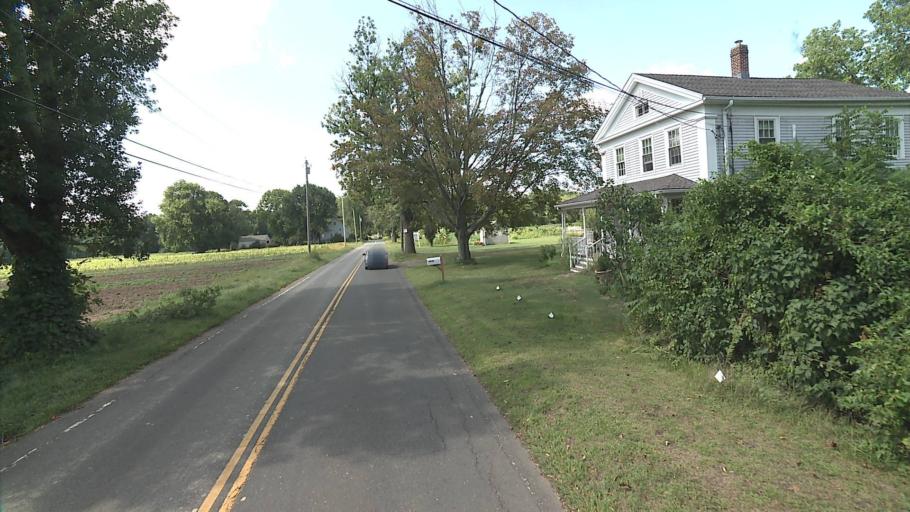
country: US
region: Connecticut
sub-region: Hartford County
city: Glastonbury Center
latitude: 41.6648
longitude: -72.6215
